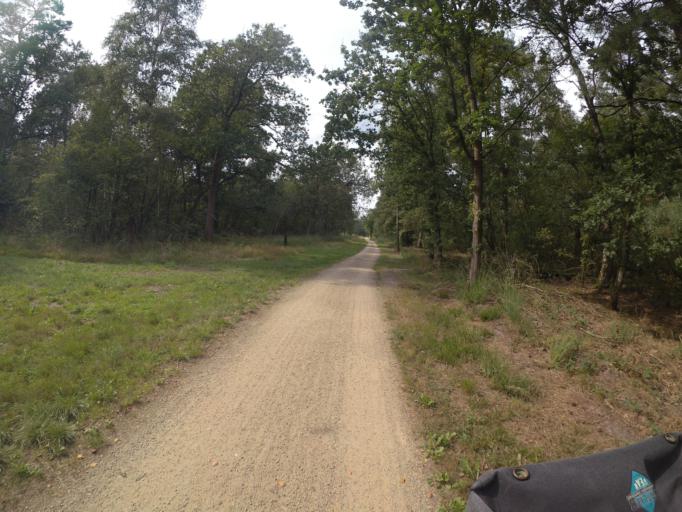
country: DE
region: North Rhine-Westphalia
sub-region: Regierungsbezirk Dusseldorf
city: Goch
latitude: 51.6188
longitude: 6.0762
